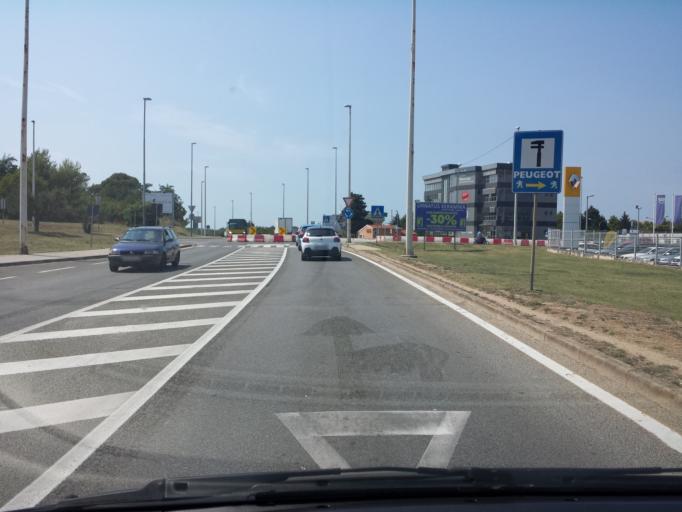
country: HR
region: Istarska
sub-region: Grad Pula
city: Pula
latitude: 44.8857
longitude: 13.8582
